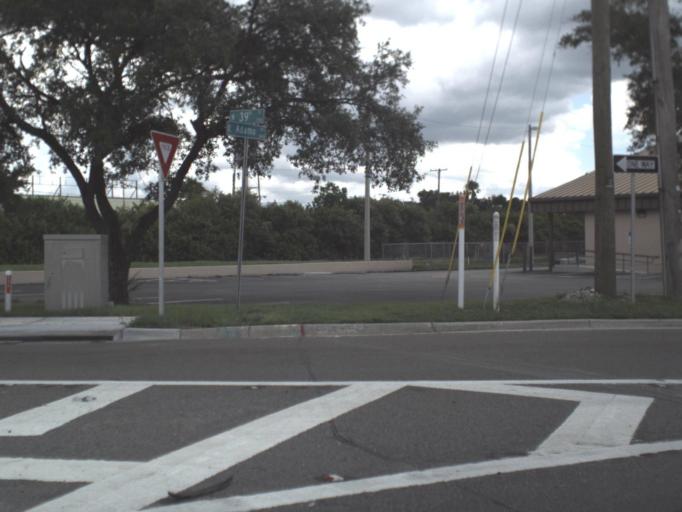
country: US
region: Florida
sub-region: Hillsborough County
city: Tampa
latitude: 27.9554
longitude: -82.4154
